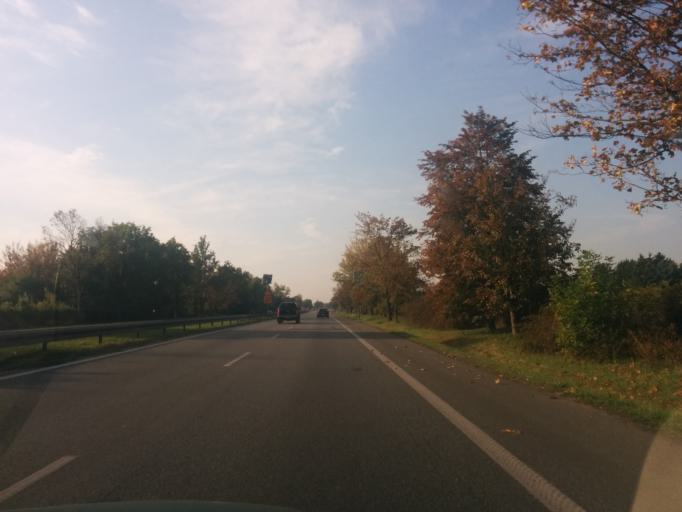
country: PL
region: Masovian Voivodeship
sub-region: Powiat piaseczynski
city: Tarczyn
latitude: 52.0332
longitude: 20.8590
